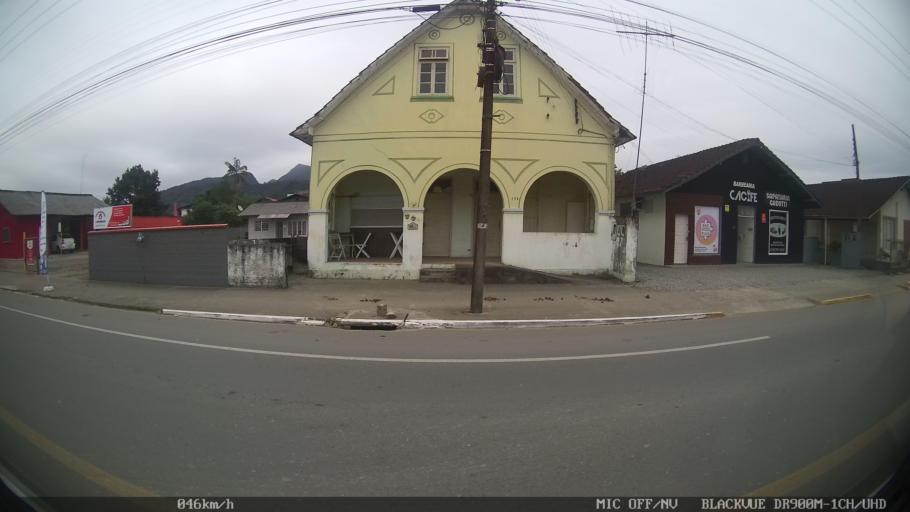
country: BR
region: Santa Catarina
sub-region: Joinville
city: Joinville
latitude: -26.2078
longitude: -48.9073
